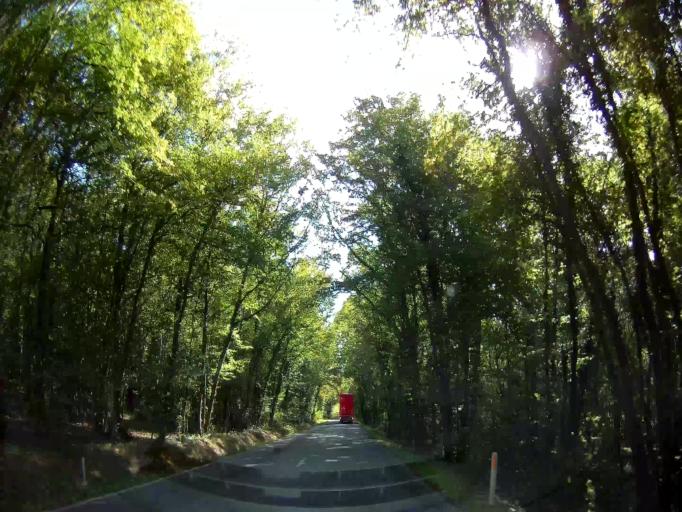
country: BE
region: Wallonia
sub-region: Province de Namur
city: Rochefort
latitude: 50.1675
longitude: 5.1645
